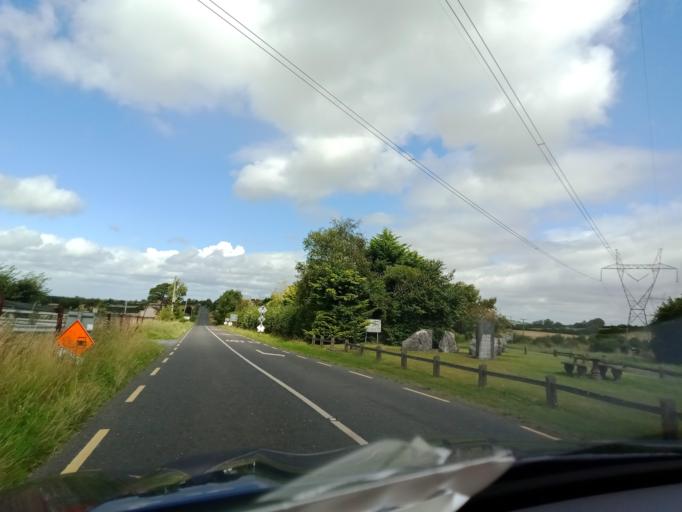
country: IE
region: Leinster
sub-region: Laois
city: Portlaoise
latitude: 52.9724
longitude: -7.2931
